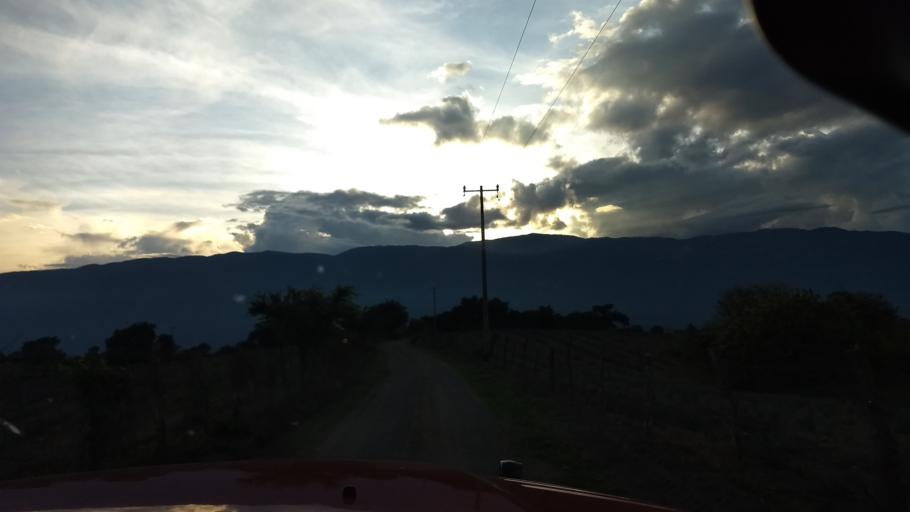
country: MX
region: Colima
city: Suchitlan
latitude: 19.4902
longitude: -103.7890
